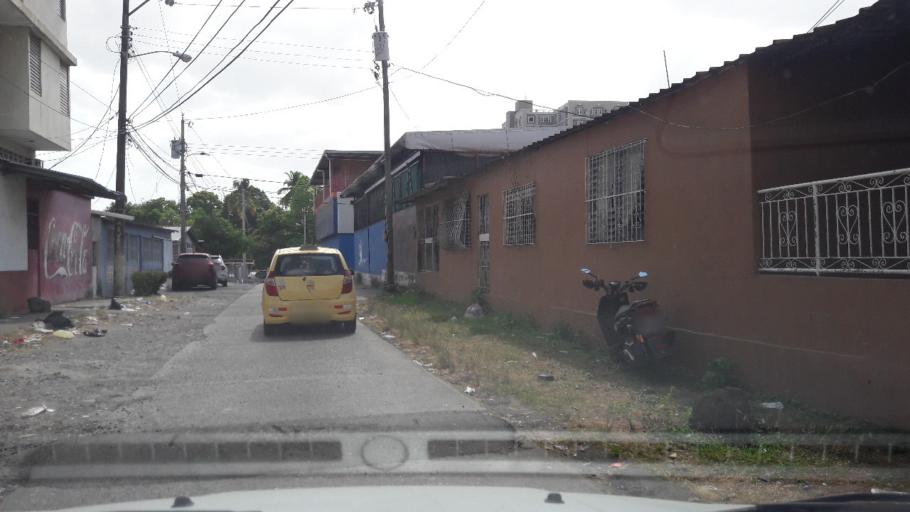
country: PA
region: Panama
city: San Miguelito
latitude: 9.0346
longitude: -79.4920
